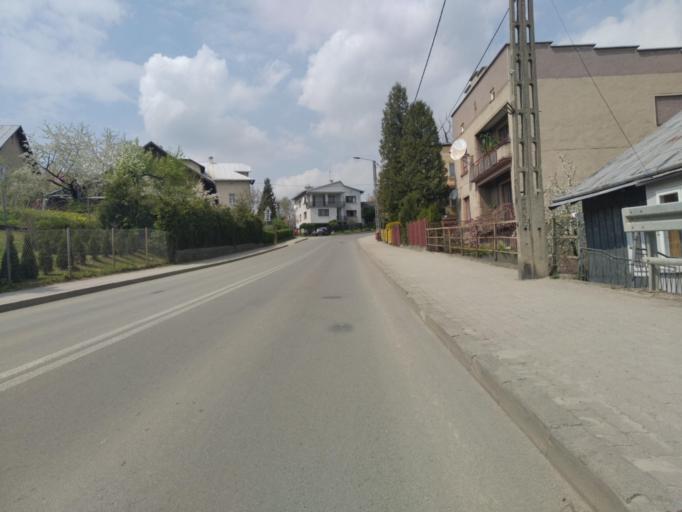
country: PL
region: Subcarpathian Voivodeship
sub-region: Powiat krosnienski
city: Rymanow
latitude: 49.5734
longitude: 21.8675
